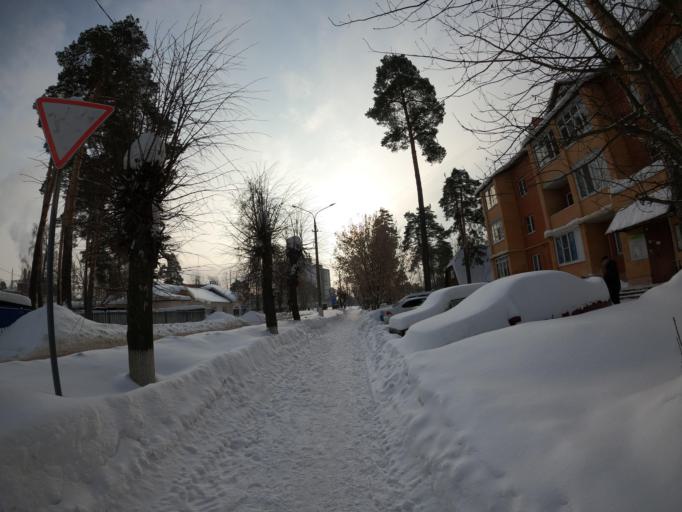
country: RU
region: Moskovskaya
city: Elektrogorsk
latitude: 55.8901
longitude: 38.7793
